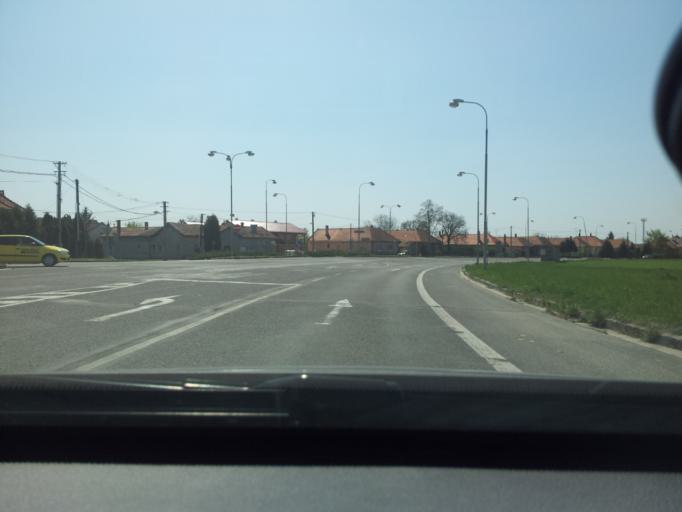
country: SK
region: Nitriansky
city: Zlate Moravce
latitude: 48.4037
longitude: 18.4119
